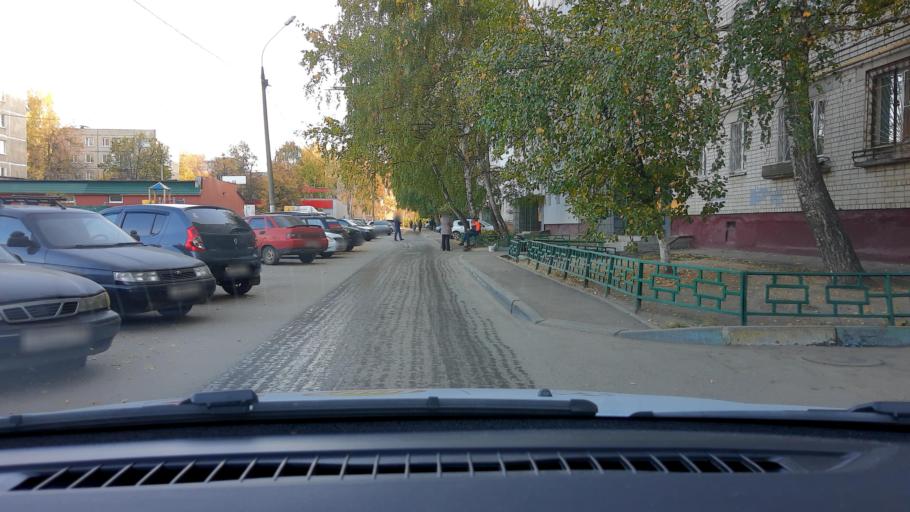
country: RU
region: Nizjnij Novgorod
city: Gorbatovka
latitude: 56.2554
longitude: 43.8805
